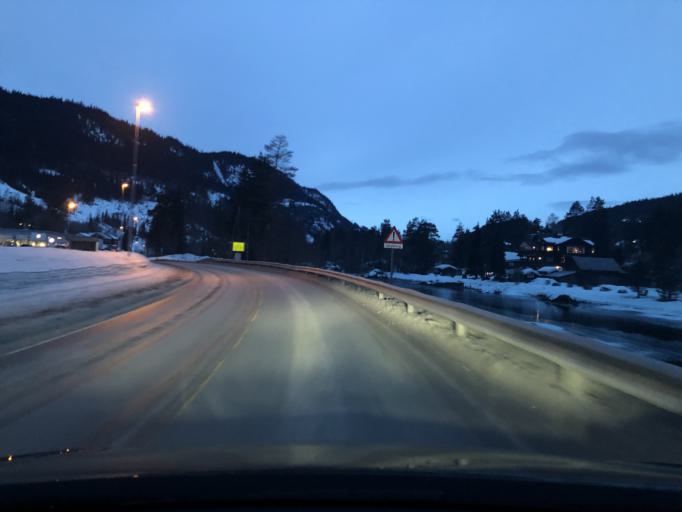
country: NO
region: Oppland
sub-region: Nord-Aurdal
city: Fagernes
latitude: 60.9895
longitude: 9.2247
